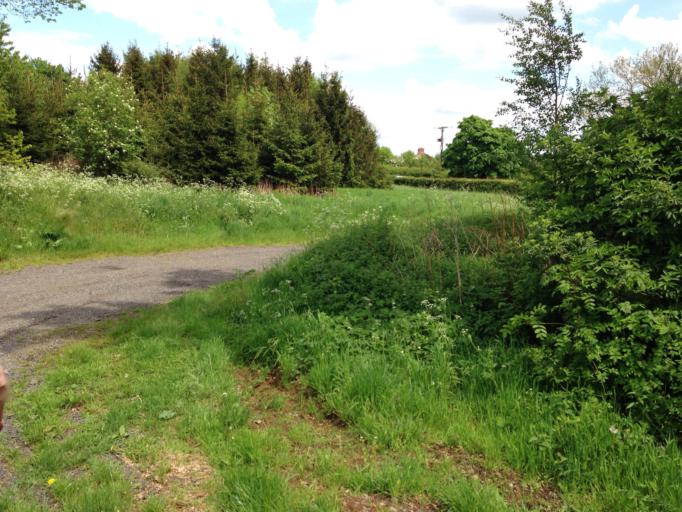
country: GB
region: England
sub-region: Northamptonshire
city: Broughton
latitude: 52.3389
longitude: -0.8306
